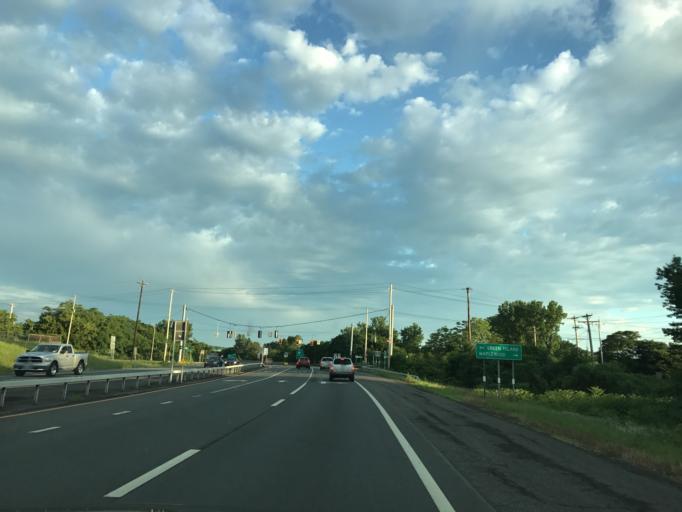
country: US
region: New York
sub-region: Albany County
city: Green Island
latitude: 42.7511
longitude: -73.6993
